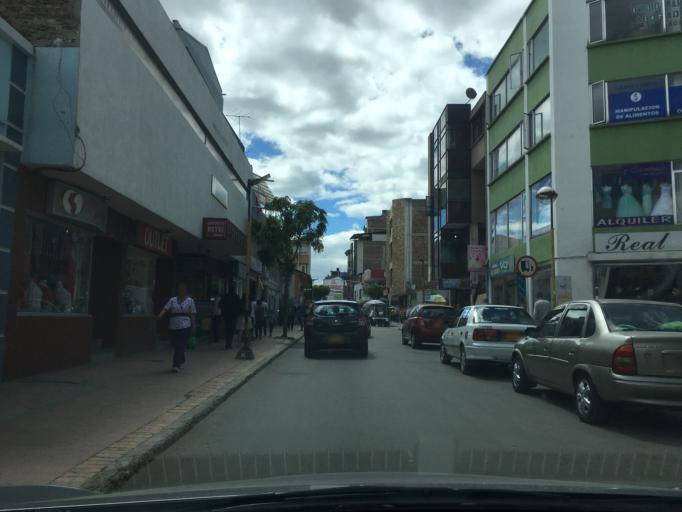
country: CO
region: Boyaca
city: Sogamoso
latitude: 5.7157
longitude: -72.9289
